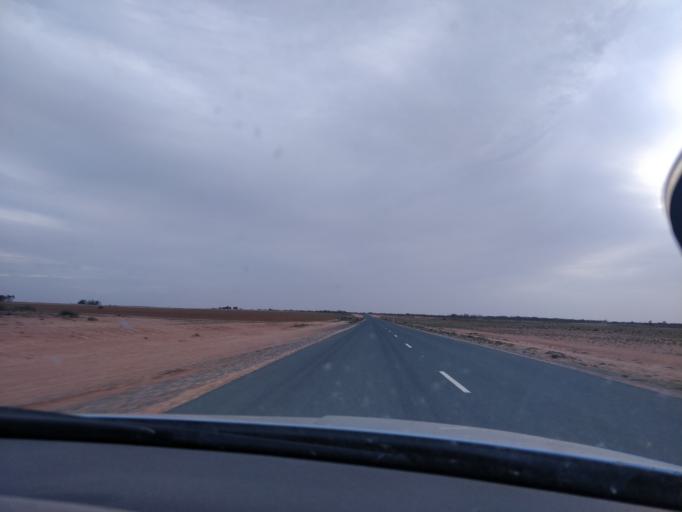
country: AU
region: New South Wales
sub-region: Wentworth
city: Gol Gol
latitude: -34.0463
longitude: 142.3357
